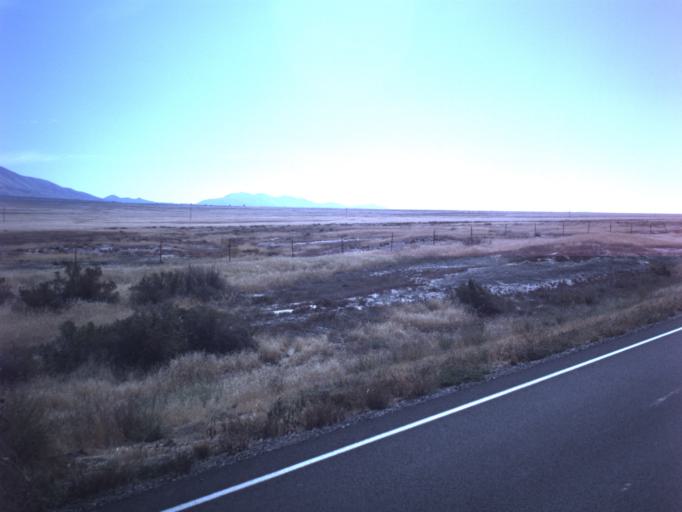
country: US
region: Utah
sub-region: Tooele County
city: Grantsville
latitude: 40.4500
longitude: -112.7483
